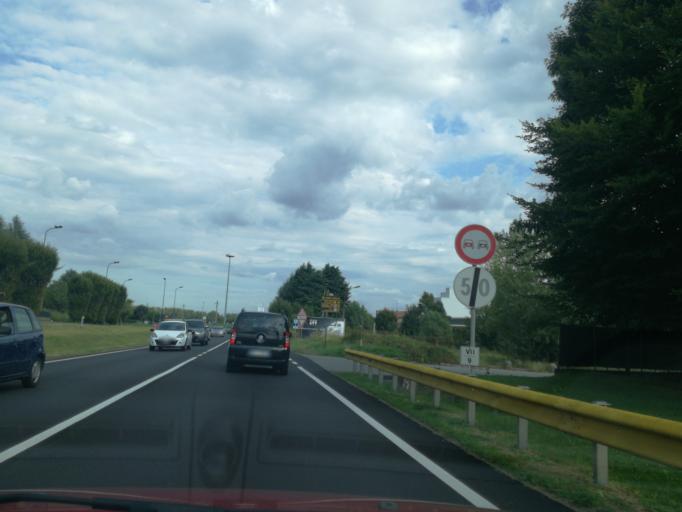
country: IT
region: Lombardy
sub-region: Provincia di Monza e Brianza
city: Bellusco
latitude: 45.6131
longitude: 9.4165
